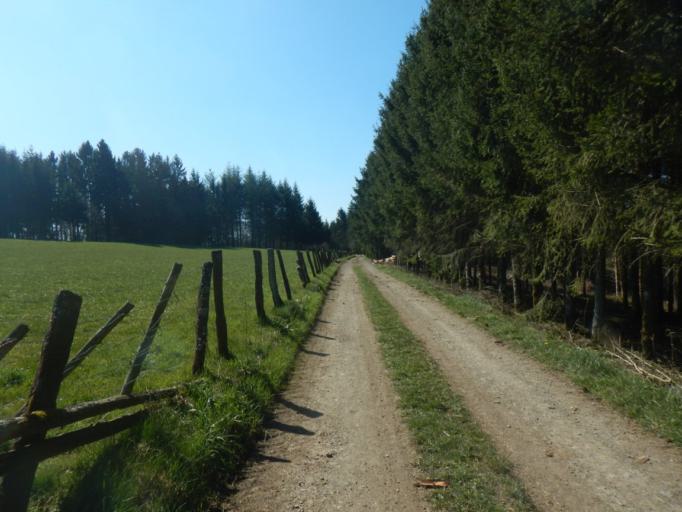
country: LU
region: Diekirch
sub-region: Canton de Clervaux
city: Troisvierges
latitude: 50.1025
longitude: 6.0289
